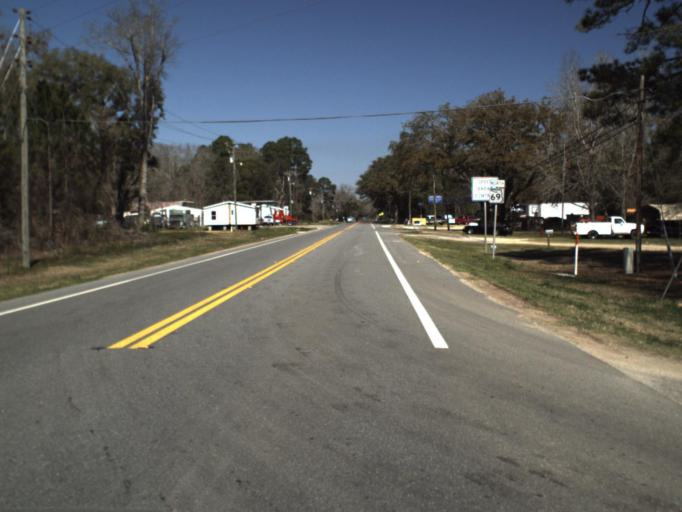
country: US
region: Florida
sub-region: Jackson County
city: Sneads
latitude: 30.7037
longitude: -85.0202
